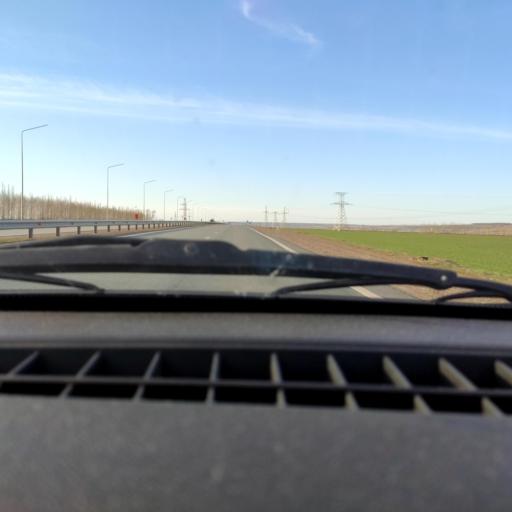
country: RU
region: Bashkortostan
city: Tolbazy
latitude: 54.2421
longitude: 55.8826
